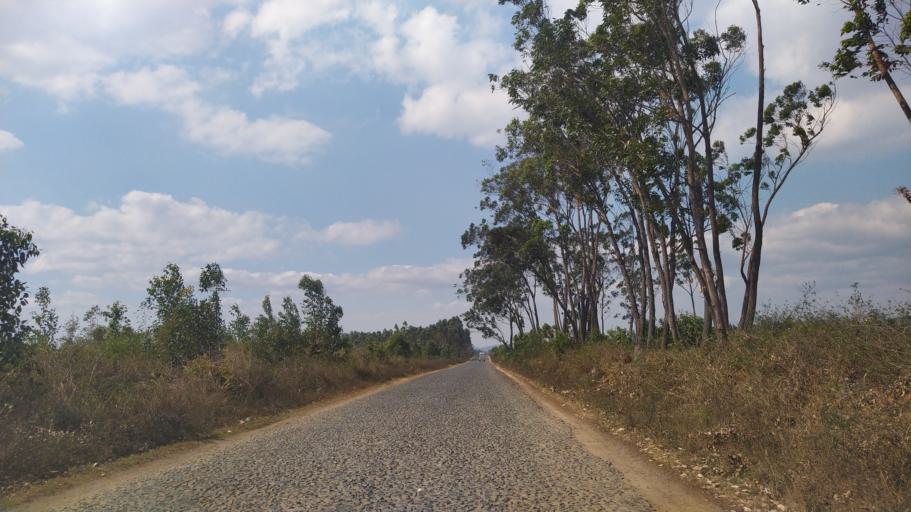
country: MG
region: Alaotra Mangoro
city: Moramanga
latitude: -18.7769
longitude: 48.2494
